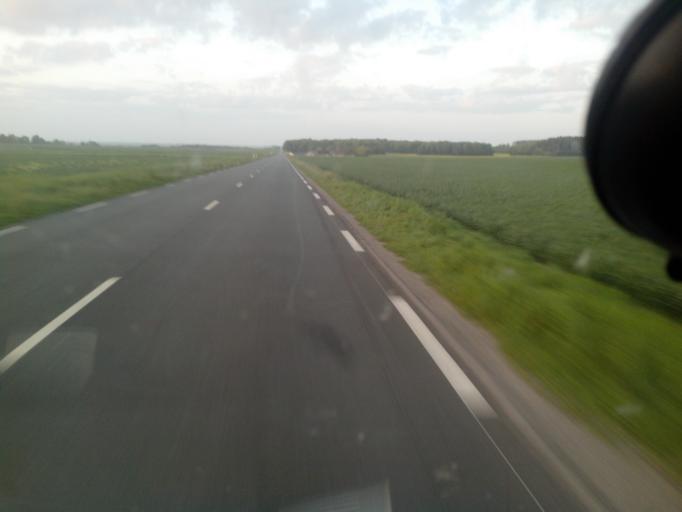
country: FR
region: Picardie
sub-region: Departement de la Somme
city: Crecy-en-Ponthieu
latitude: 50.2082
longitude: 1.9037
